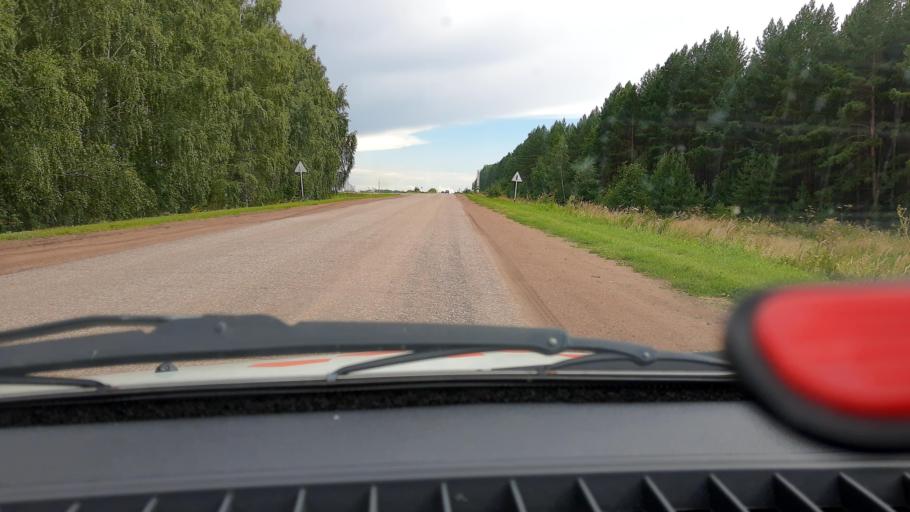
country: RU
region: Bashkortostan
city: Semiletka
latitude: 55.3722
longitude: 54.5995
